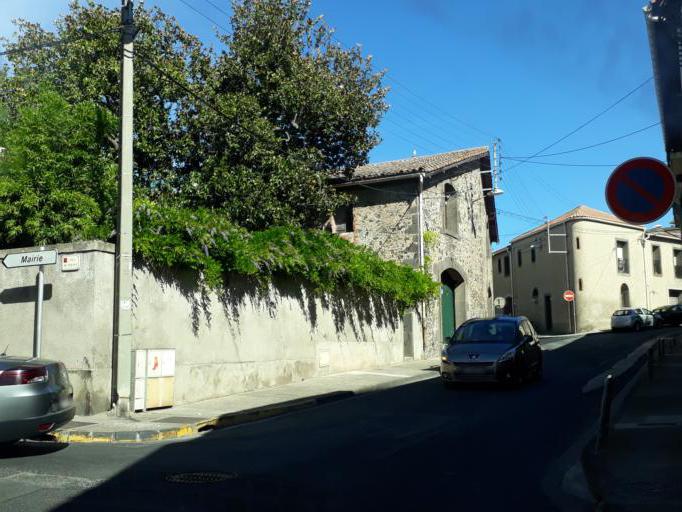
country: FR
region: Languedoc-Roussillon
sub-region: Departement de l'Herault
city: Agde
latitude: 43.3139
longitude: 3.4734
